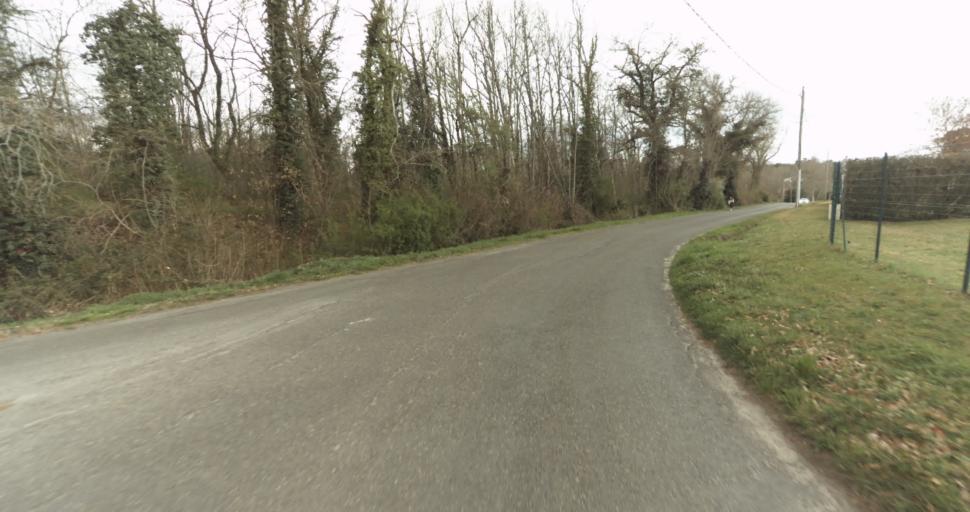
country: FR
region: Aquitaine
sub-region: Departement des Landes
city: Sarbazan
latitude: 44.0283
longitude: -0.3162
